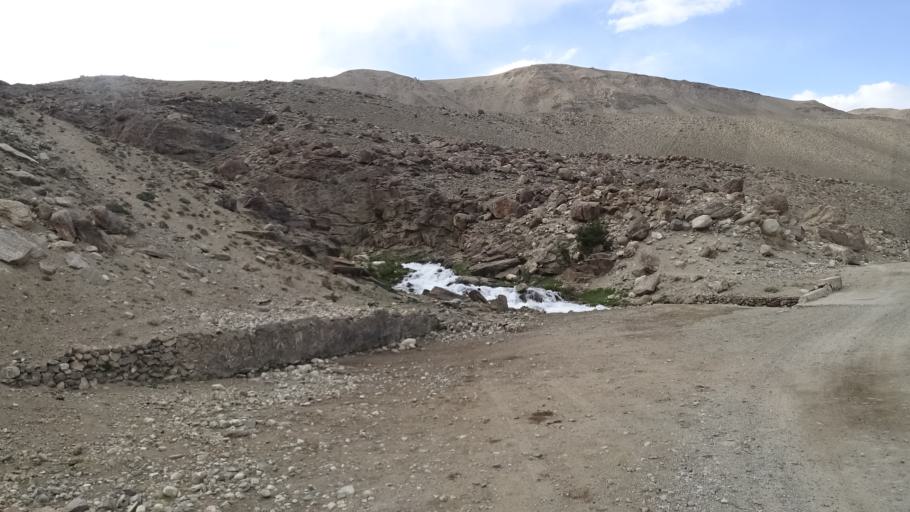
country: AF
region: Badakhshan
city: Khandud
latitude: 37.2197
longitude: 72.7868
